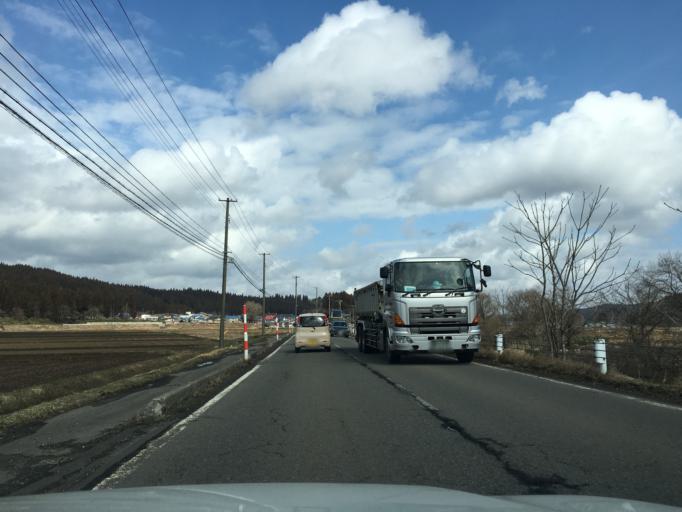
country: JP
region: Akita
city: Takanosu
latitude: 40.0393
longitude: 140.2791
